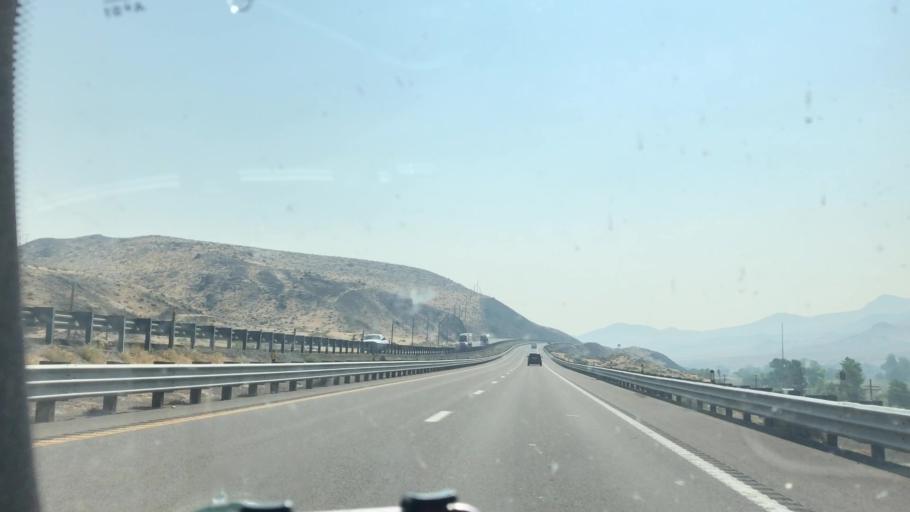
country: US
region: Nevada
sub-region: Lyon County
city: Fernley
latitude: 39.5913
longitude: -119.4112
